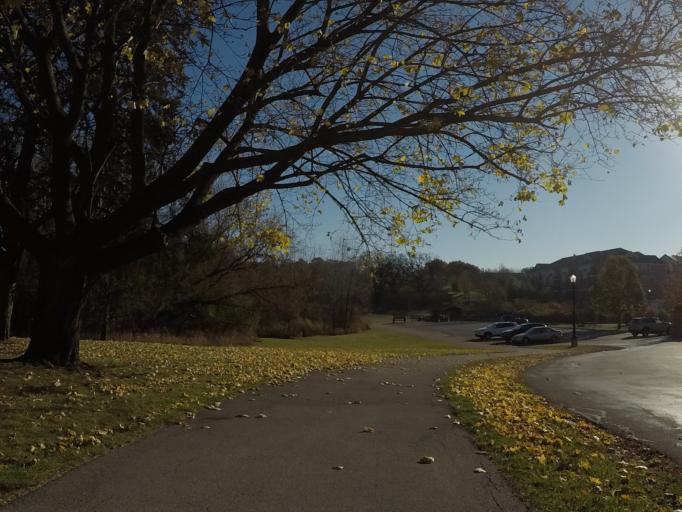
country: US
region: Wisconsin
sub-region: Dane County
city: Cottage Grove
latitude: 43.0764
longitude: -89.1996
